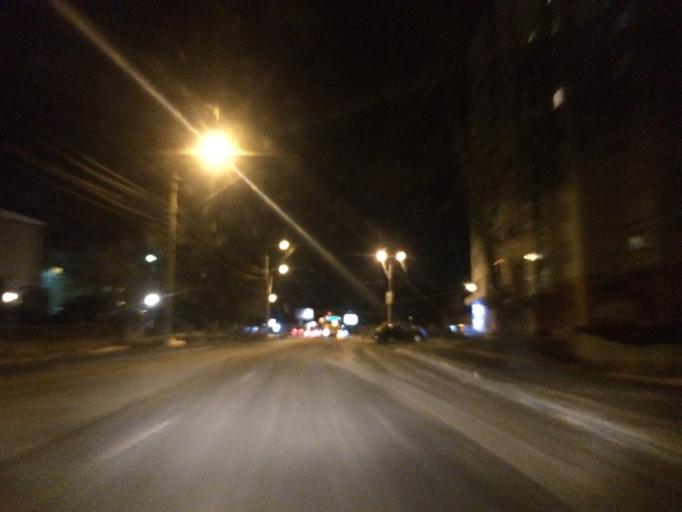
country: RU
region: Tula
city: Mendeleyevskiy
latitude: 54.1611
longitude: 37.5996
